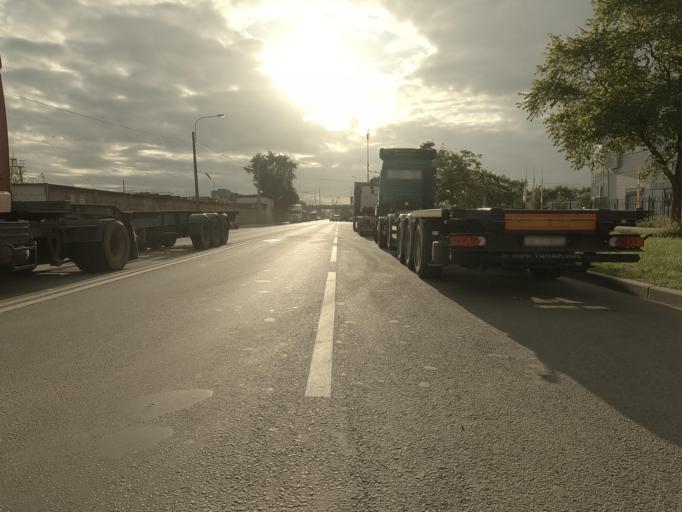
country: RU
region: St.-Petersburg
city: Avtovo
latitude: 59.8655
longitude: 30.2468
